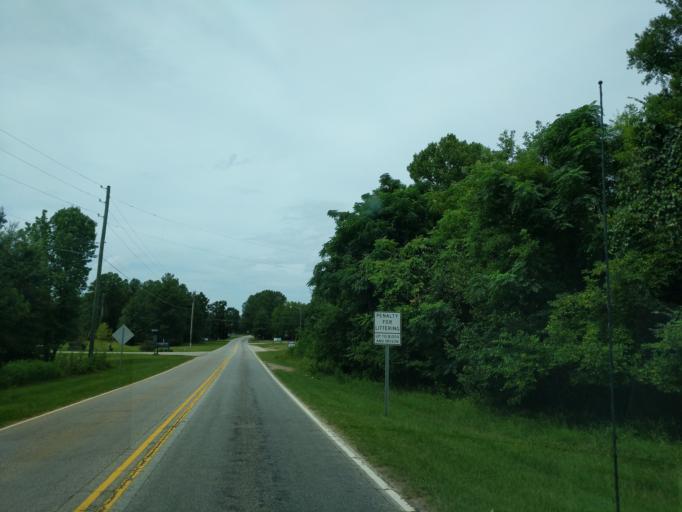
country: US
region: South Carolina
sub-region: Abbeville County
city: Calhoun Falls
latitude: 34.0935
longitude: -82.5982
